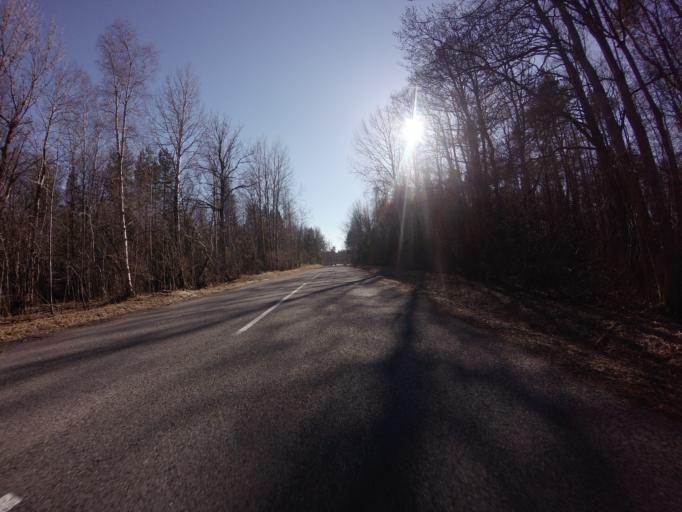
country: EE
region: Saare
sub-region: Kuressaare linn
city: Kuressaare
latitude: 58.4912
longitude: 22.3042
